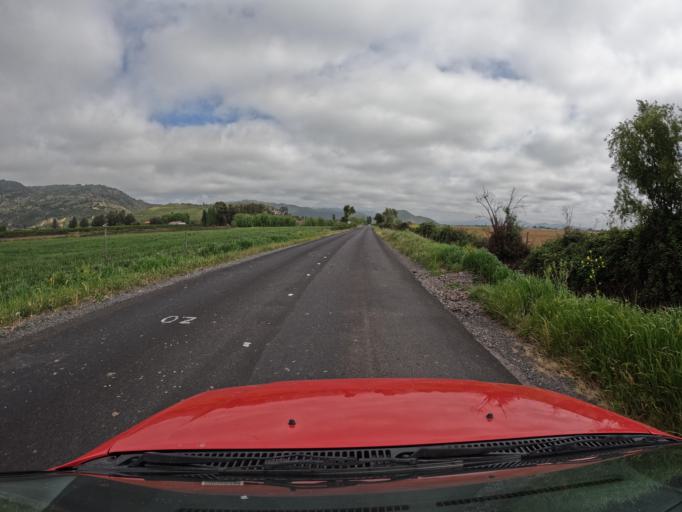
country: CL
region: O'Higgins
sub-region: Provincia de Colchagua
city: Santa Cruz
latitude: -34.6655
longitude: -71.3934
